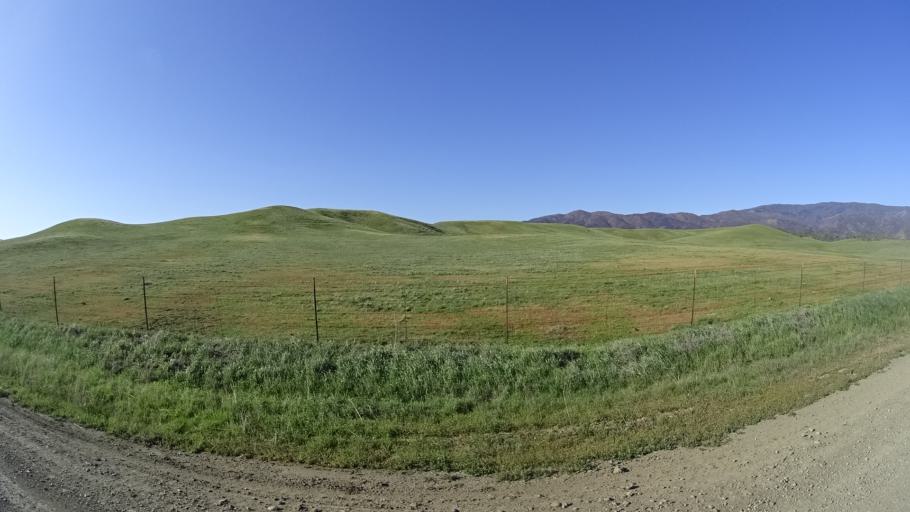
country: US
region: California
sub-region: Tehama County
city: Rancho Tehama Reserve
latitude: 39.7958
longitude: -122.5464
